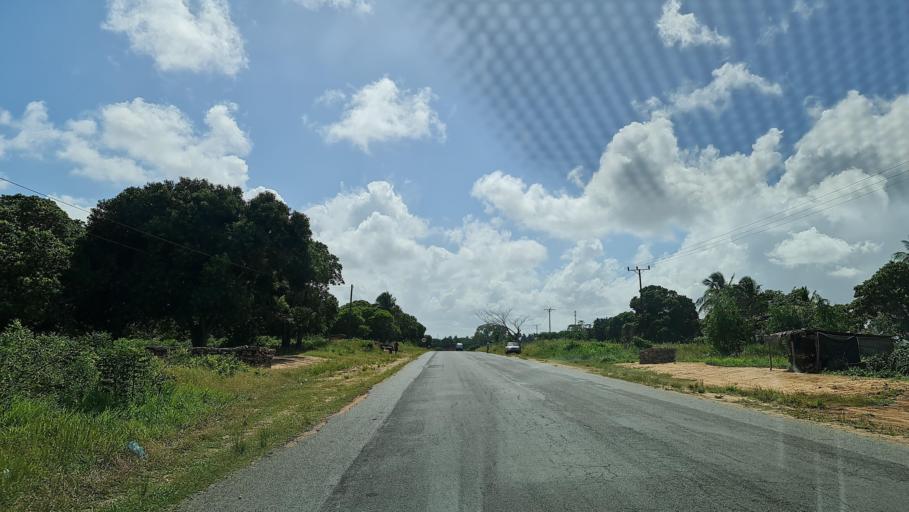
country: MZ
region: Gaza
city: Manjacaze
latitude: -24.6749
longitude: 34.5695
